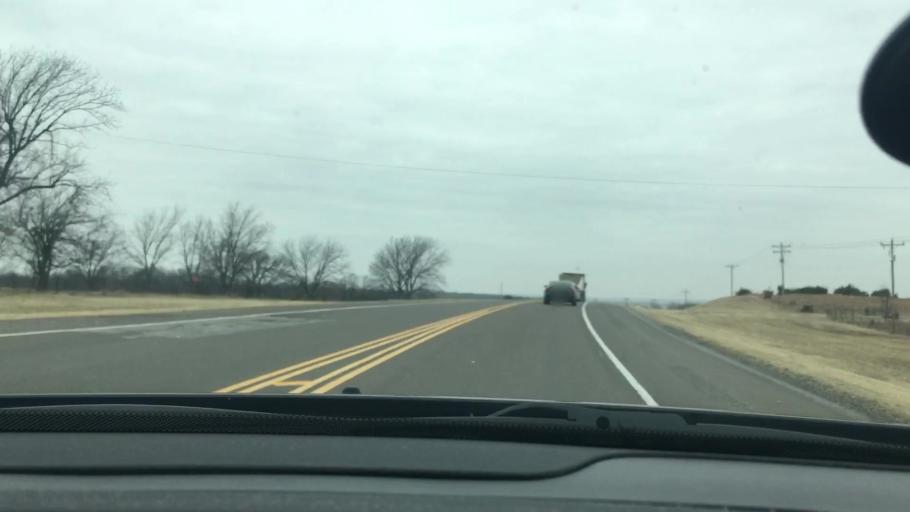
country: US
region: Oklahoma
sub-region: Murray County
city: Davis
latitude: 34.5111
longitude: -97.1971
